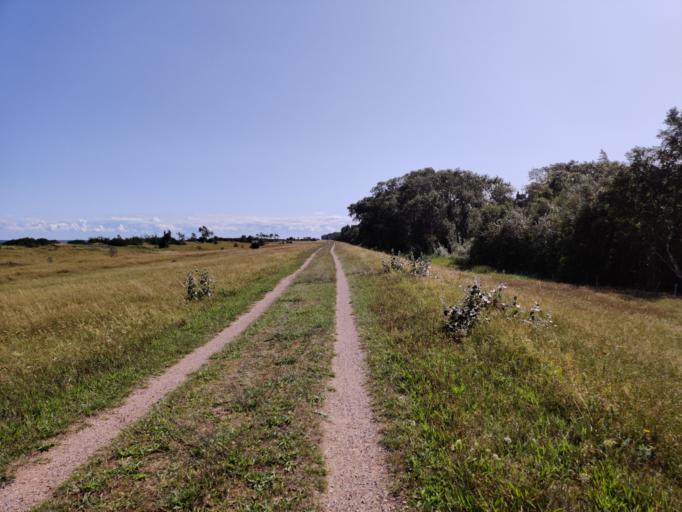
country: DK
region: Zealand
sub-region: Guldborgsund Kommune
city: Nykobing Falster
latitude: 54.6238
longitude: 11.9625
